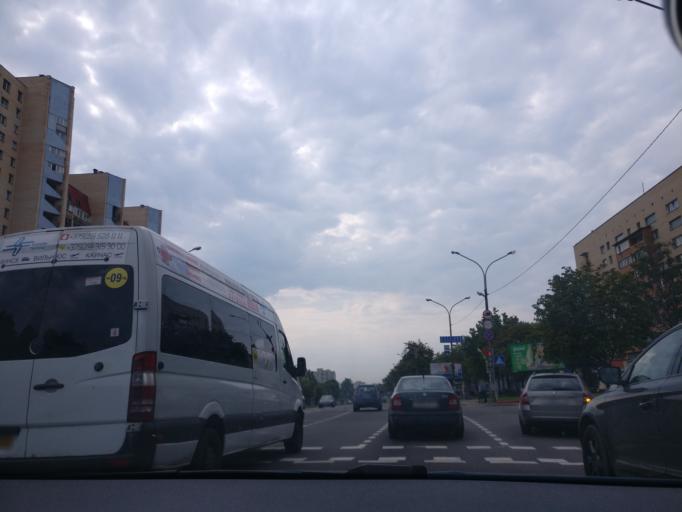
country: BY
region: Minsk
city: Minsk
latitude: 53.9425
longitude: 27.6085
